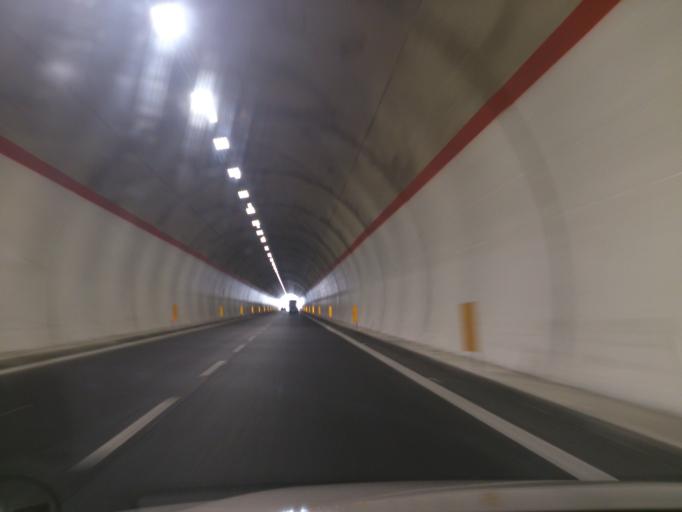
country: IT
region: Calabria
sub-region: Provincia di Reggio Calabria
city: Roccella Ionica
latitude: 38.3291
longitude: 16.4020
